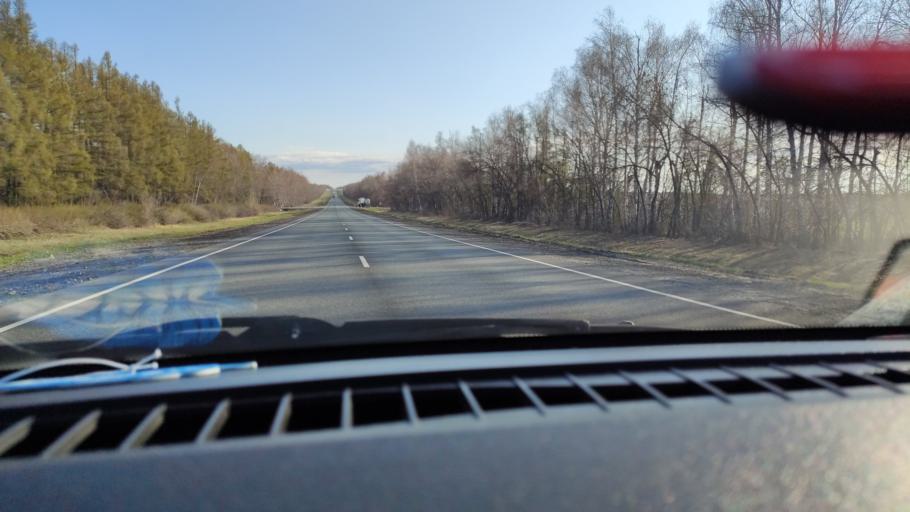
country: RU
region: Saratov
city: Khvalynsk
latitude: 52.5737
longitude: 48.1064
